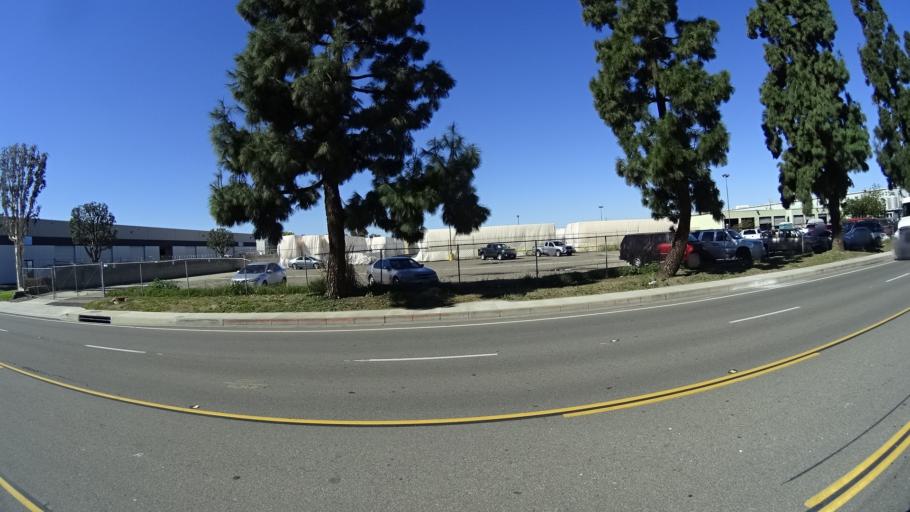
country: US
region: California
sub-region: Orange County
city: Orange
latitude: 33.8203
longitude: -117.8620
